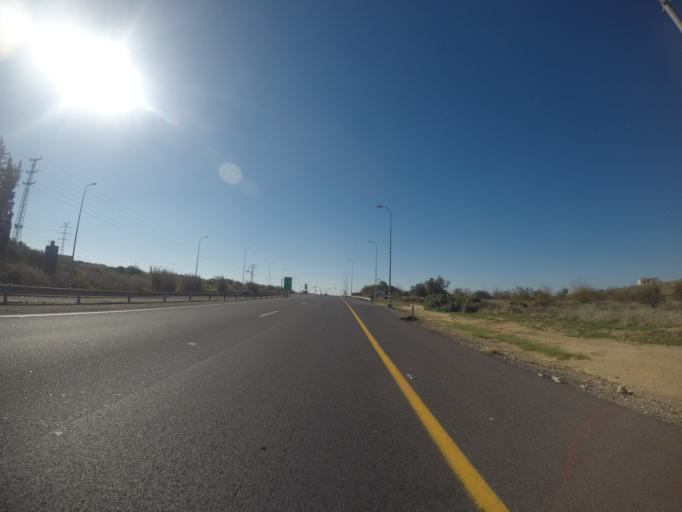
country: IL
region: Southern District
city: Ashdod
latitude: 31.7552
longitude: 34.6642
